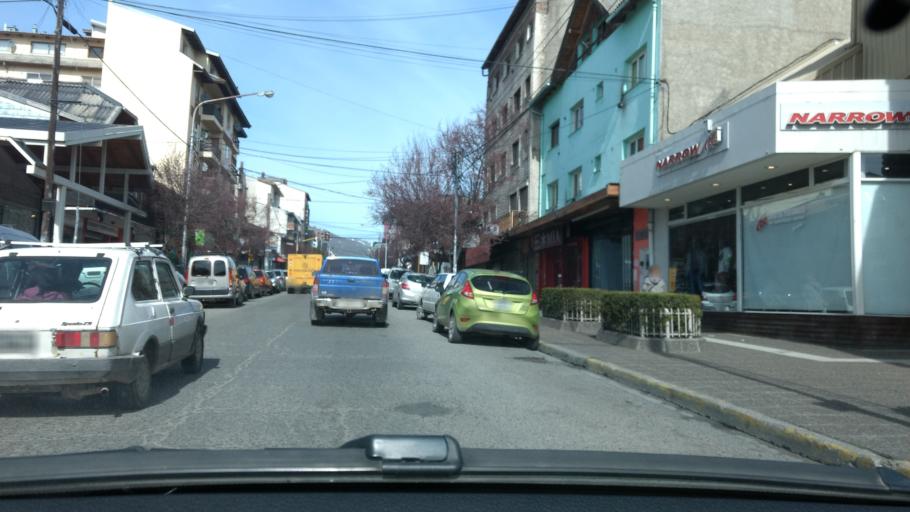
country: AR
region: Rio Negro
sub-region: Departamento de Bariloche
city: San Carlos de Bariloche
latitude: -41.1373
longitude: -71.2975
